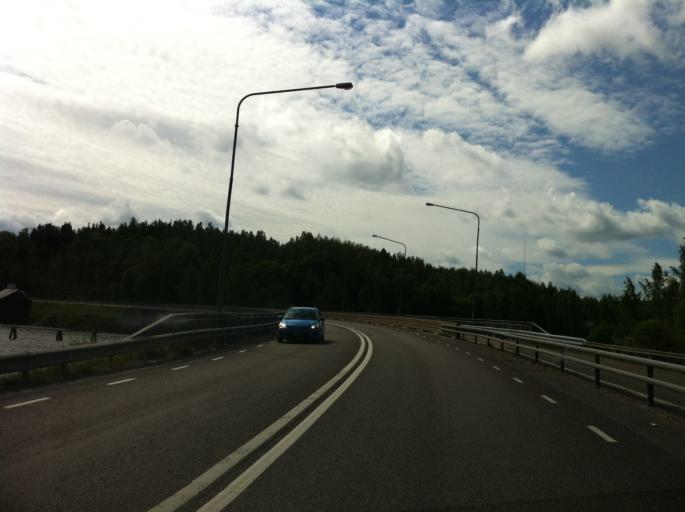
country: SE
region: Vaermland
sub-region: Grums Kommun
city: Slottsbron
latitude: 59.3325
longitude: 13.1007
